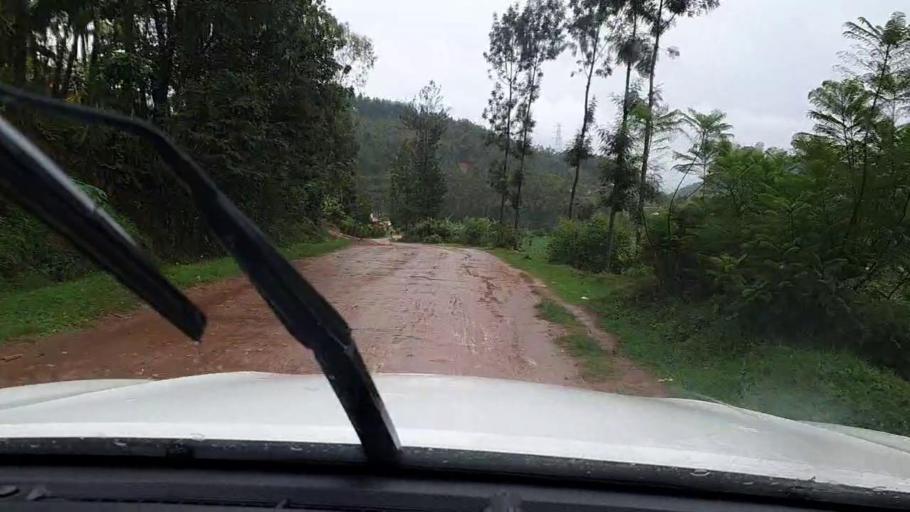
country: RW
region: Northern Province
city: Byumba
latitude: -1.7254
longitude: 29.9326
